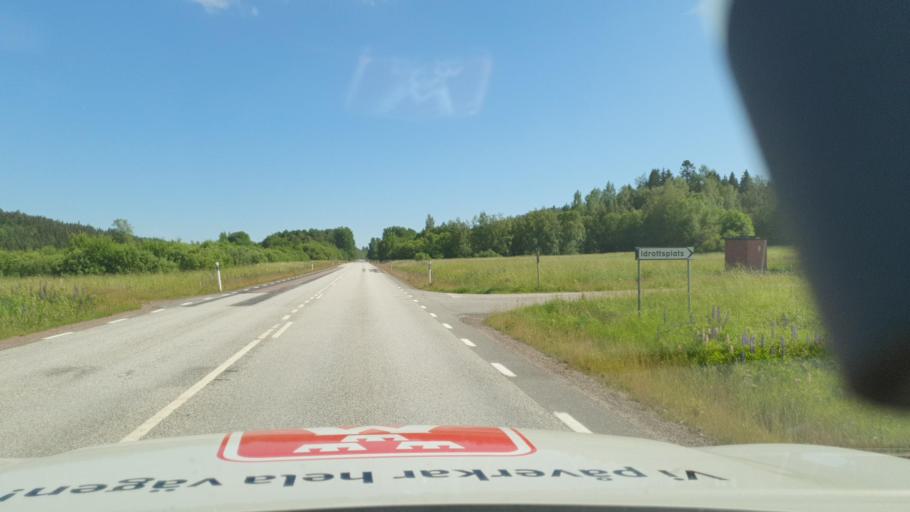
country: SE
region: Vaermland
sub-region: Storfors Kommun
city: Storfors
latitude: 59.5324
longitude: 14.2940
